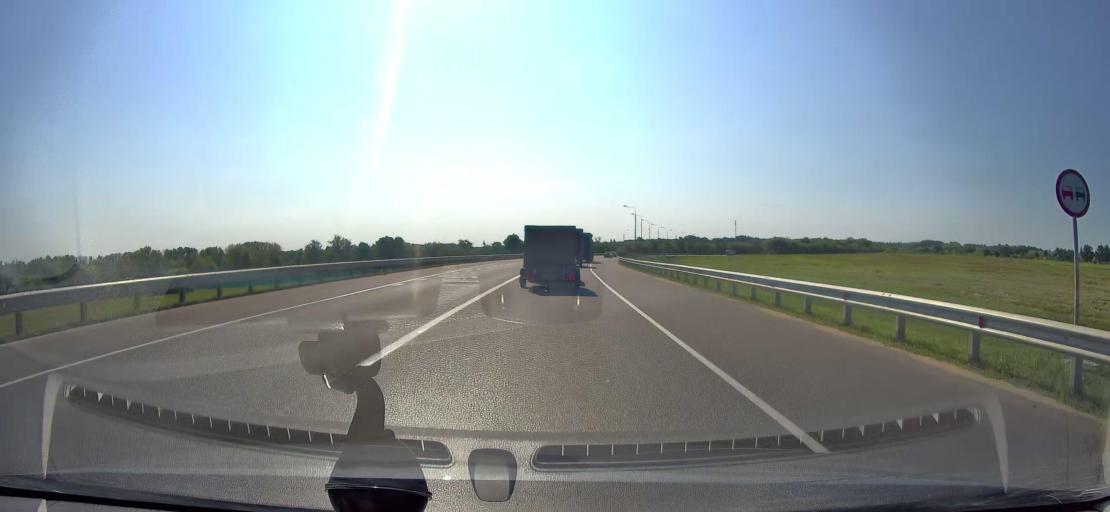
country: RU
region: Orjol
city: Kromy
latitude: 52.6485
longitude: 35.7410
